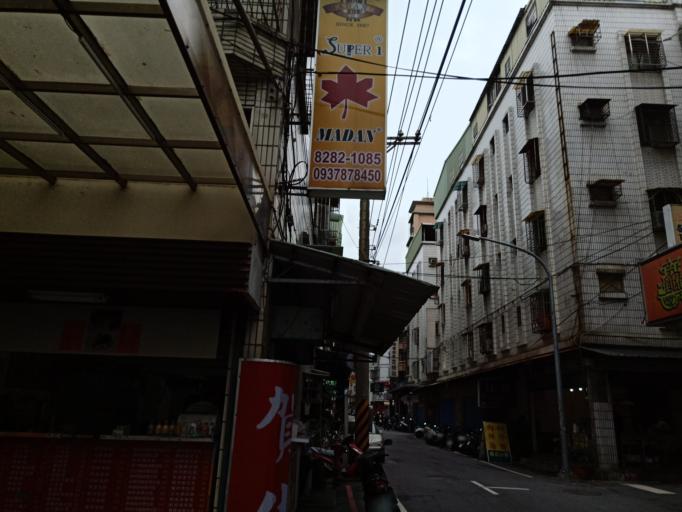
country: TW
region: Taipei
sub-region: Taipei
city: Banqiao
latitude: 25.0917
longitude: 121.4592
